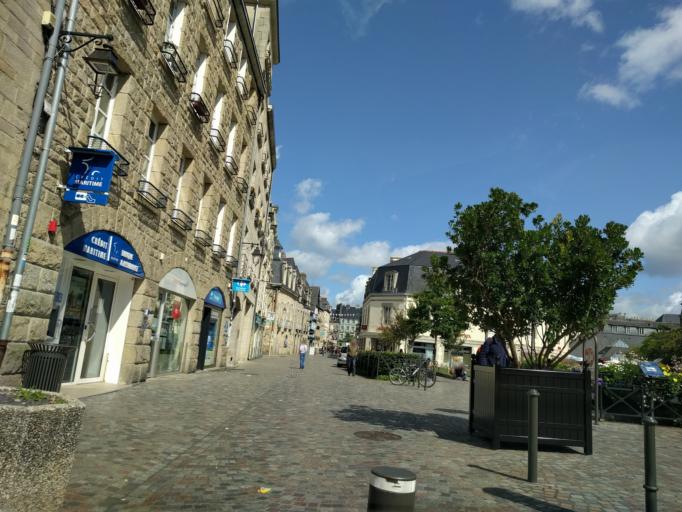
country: FR
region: Brittany
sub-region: Departement du Finistere
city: Quimper
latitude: 47.9944
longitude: -4.1060
